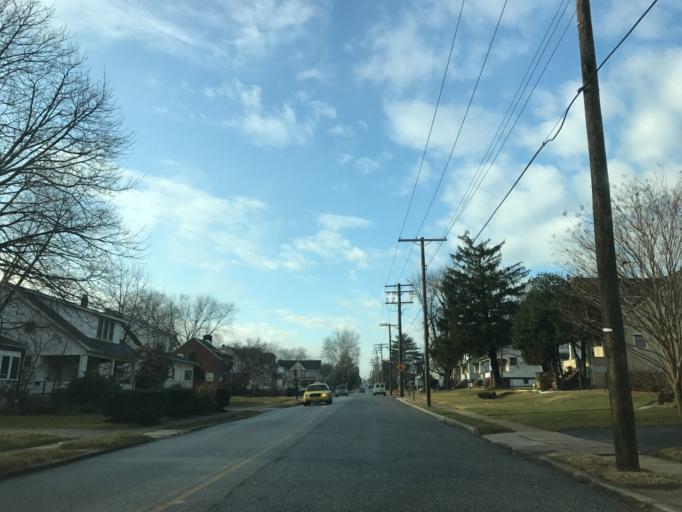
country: US
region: Maryland
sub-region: Baltimore County
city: Parkville
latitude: 39.3545
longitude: -76.5501
